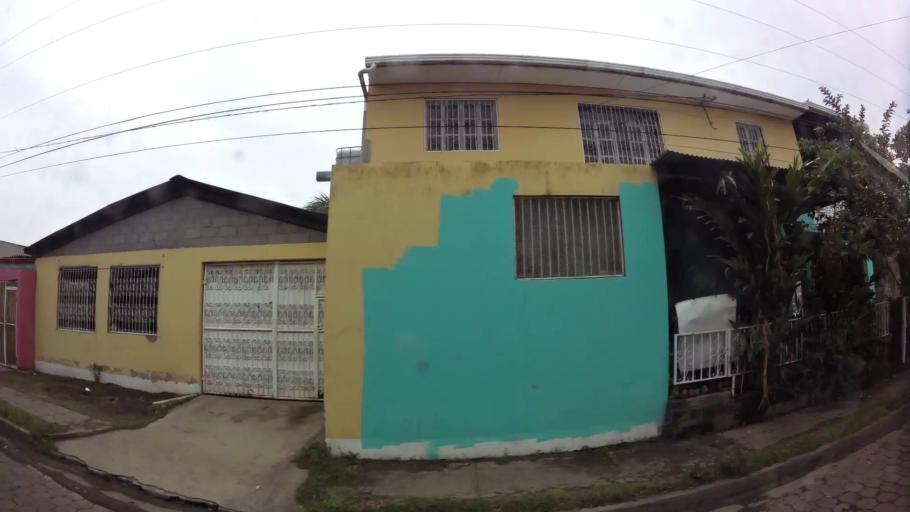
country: NI
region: Granada
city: Nandaime
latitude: 11.7591
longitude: -86.0573
